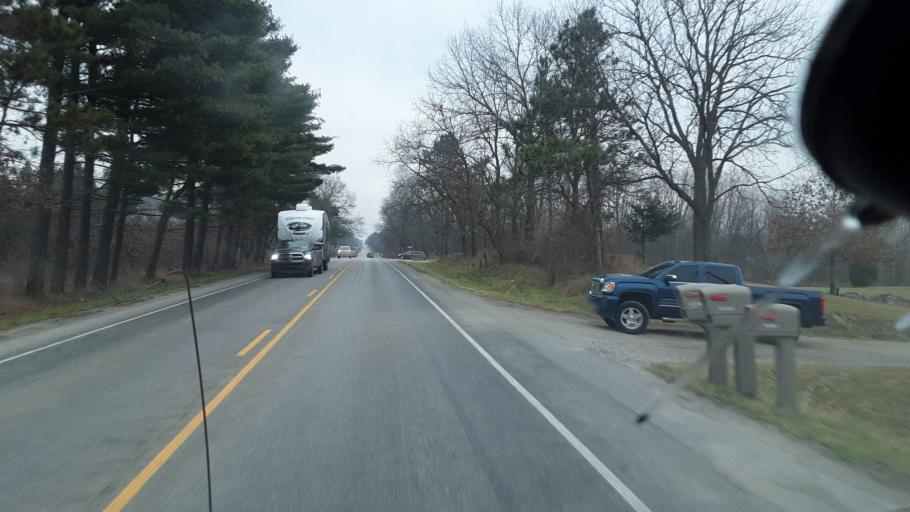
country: US
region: Indiana
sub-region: Elkhart County
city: Middlebury
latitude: 41.7258
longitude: -85.6776
